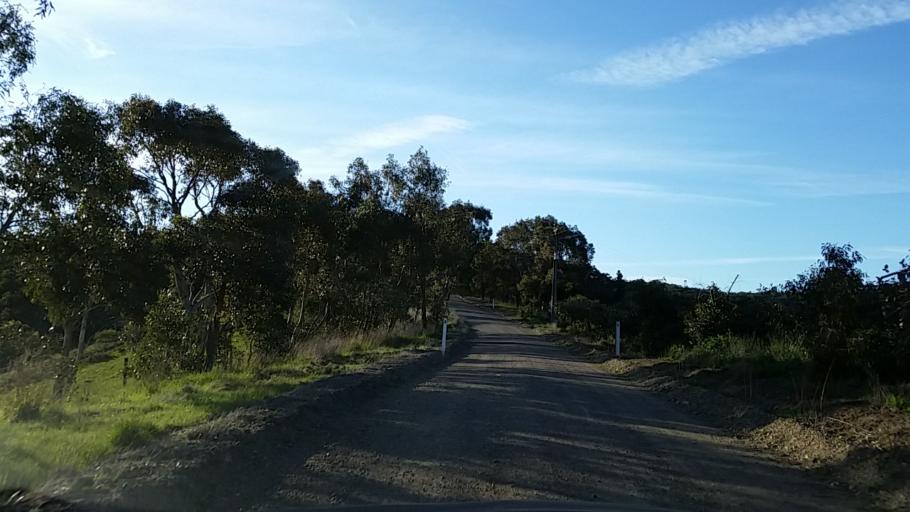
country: AU
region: South Australia
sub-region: Mount Barker
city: Meadows
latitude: -35.2394
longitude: 138.7548
